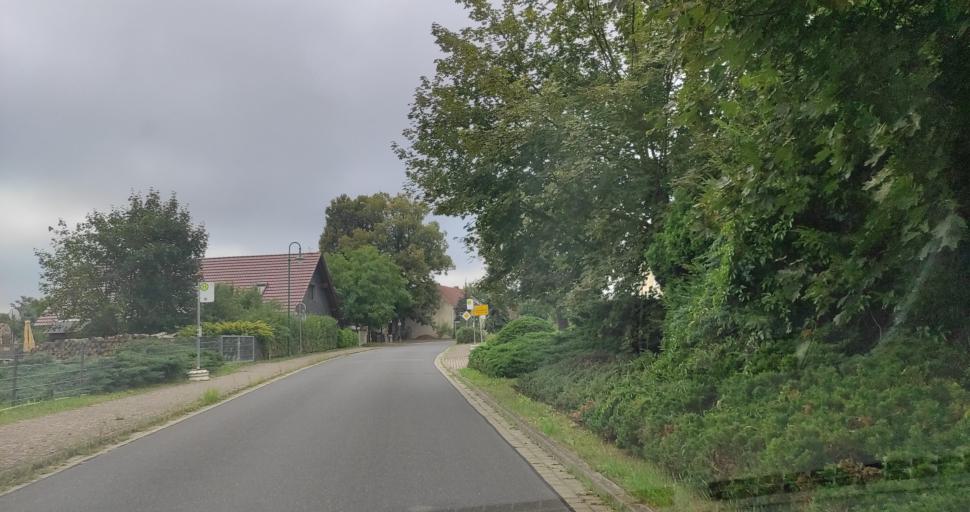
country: DE
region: Brandenburg
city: Heinersbruck
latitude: 51.7462
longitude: 14.5449
